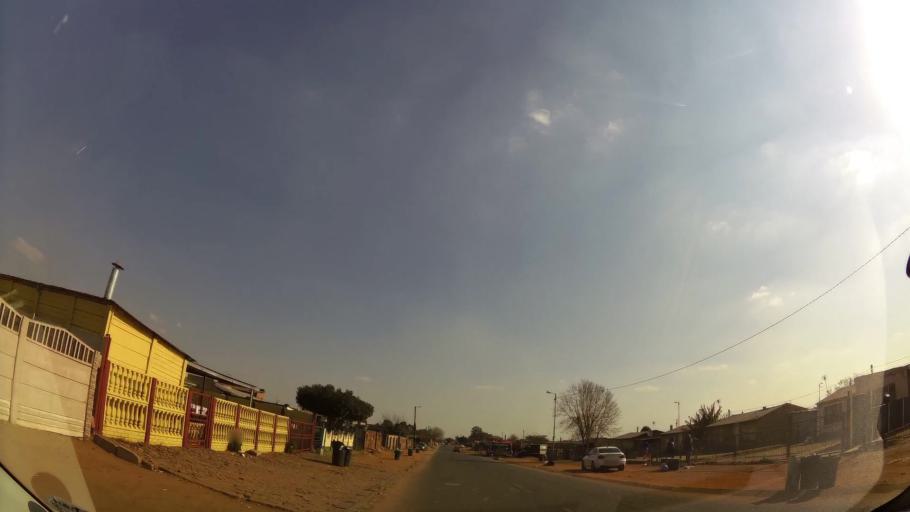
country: ZA
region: Gauteng
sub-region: Ekurhuleni Metropolitan Municipality
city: Brakpan
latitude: -26.1565
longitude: 28.4074
